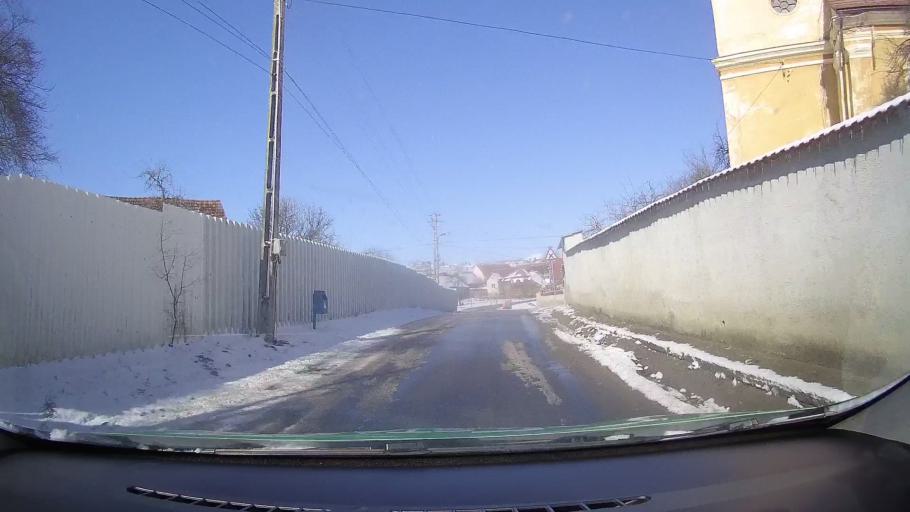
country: RO
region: Sibiu
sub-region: Comuna Avrig
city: Avrig
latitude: 45.7620
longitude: 24.3881
